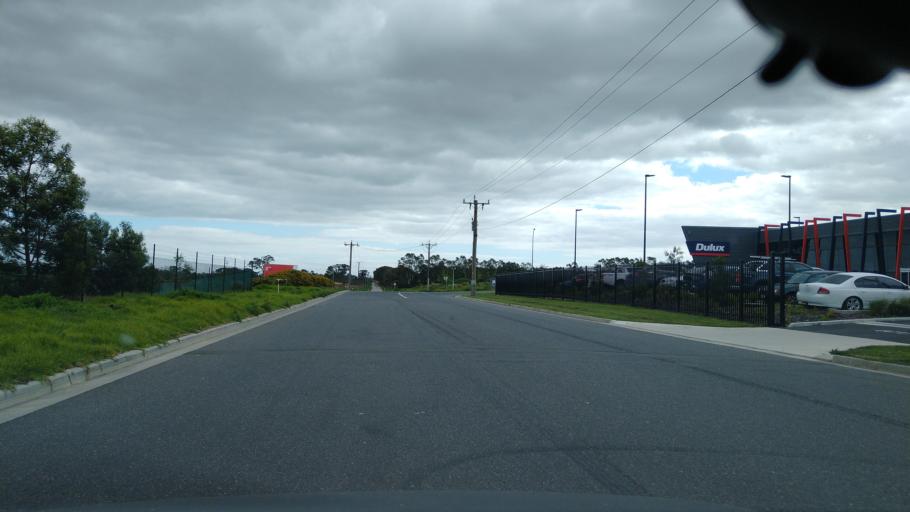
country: AU
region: Victoria
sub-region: Casey
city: Hampton Park
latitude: -38.0477
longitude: 145.2395
